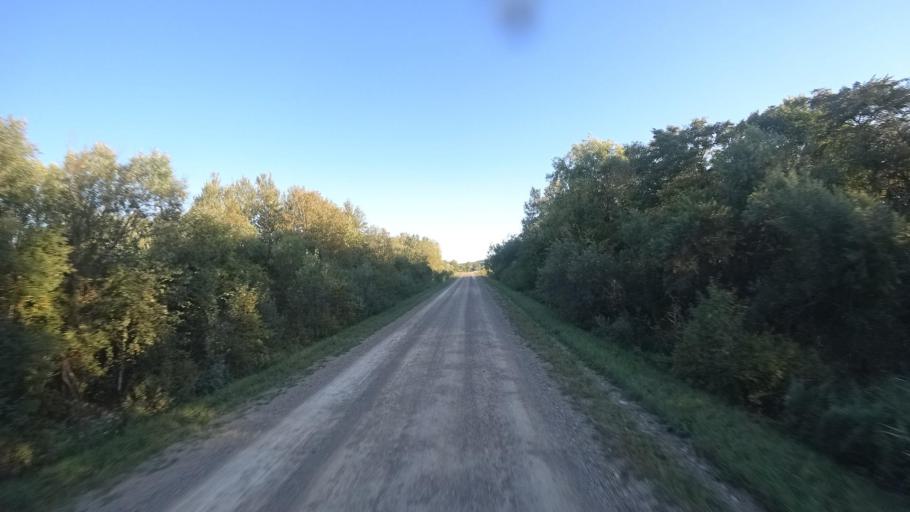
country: RU
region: Primorskiy
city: Kirovskiy
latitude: 44.7825
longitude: 133.6255
